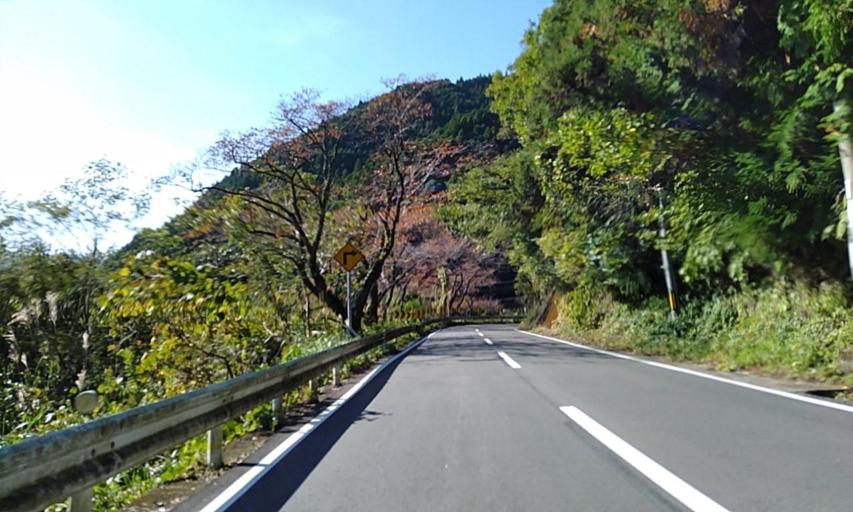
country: JP
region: Wakayama
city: Iwade
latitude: 34.0852
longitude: 135.3576
